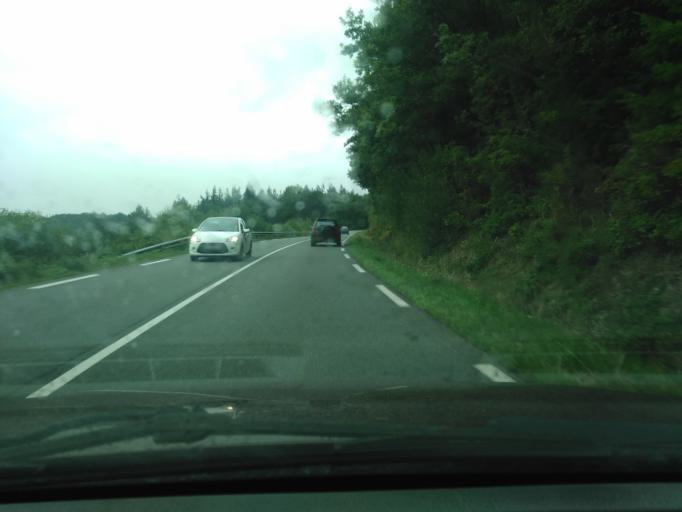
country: FR
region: Pays de la Loire
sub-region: Departement de la Vendee
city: Bournezeau
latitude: 46.5918
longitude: -1.1212
